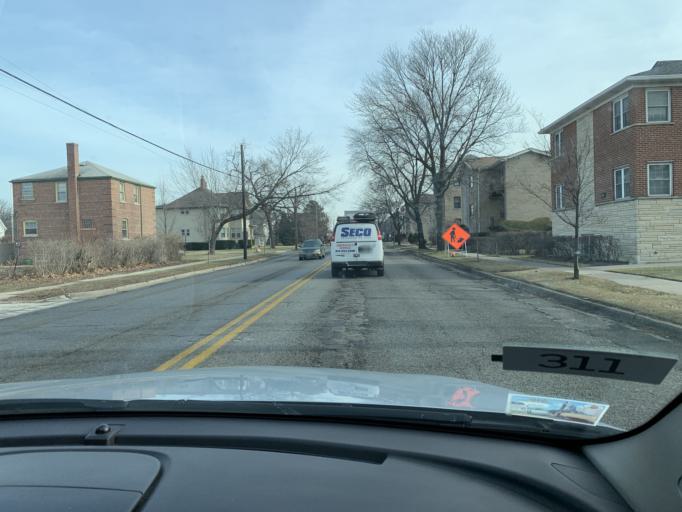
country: US
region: Illinois
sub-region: Cook County
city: Park Ridge
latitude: 42.0108
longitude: -87.8450
